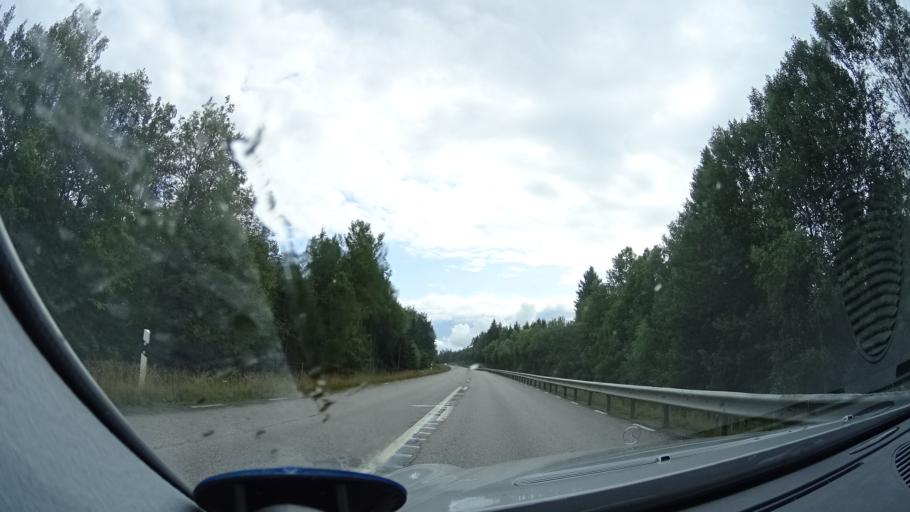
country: SE
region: Blekinge
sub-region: Karlshamns Kommun
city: Svangsta
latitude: 56.2567
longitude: 14.8338
